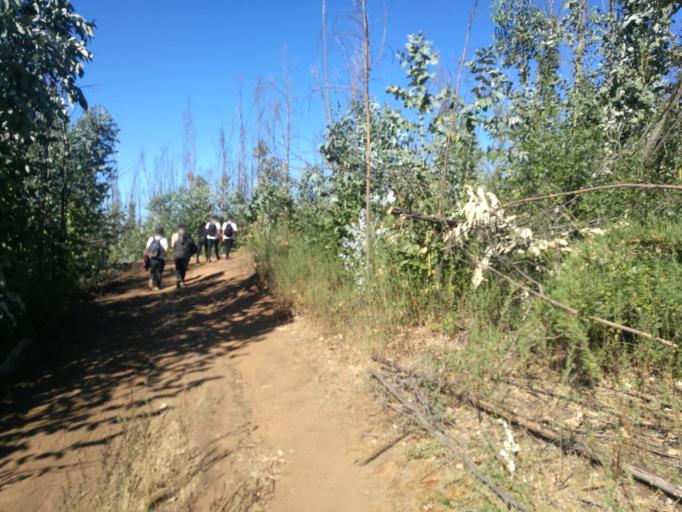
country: CL
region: Valparaiso
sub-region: Provincia de Valparaiso
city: Valparaiso
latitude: -33.0709
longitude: -71.6485
